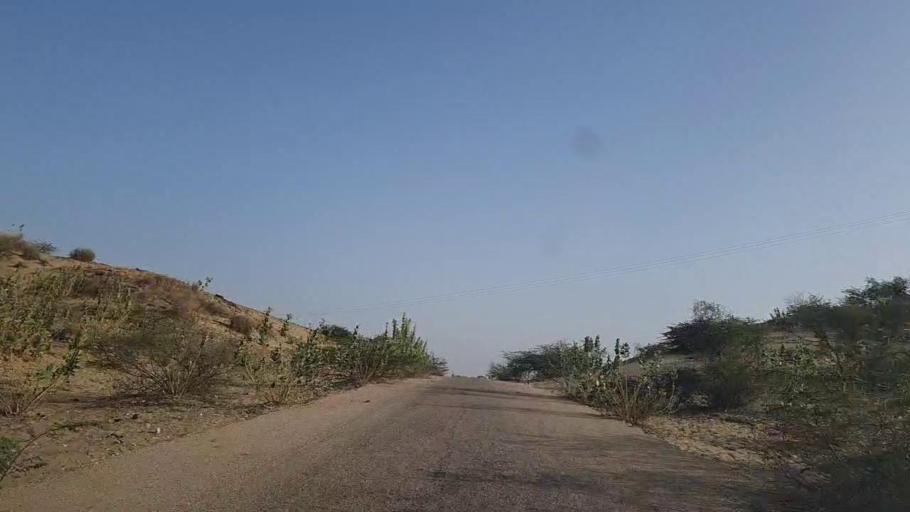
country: PK
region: Sindh
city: Diplo
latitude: 24.6075
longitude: 69.3782
